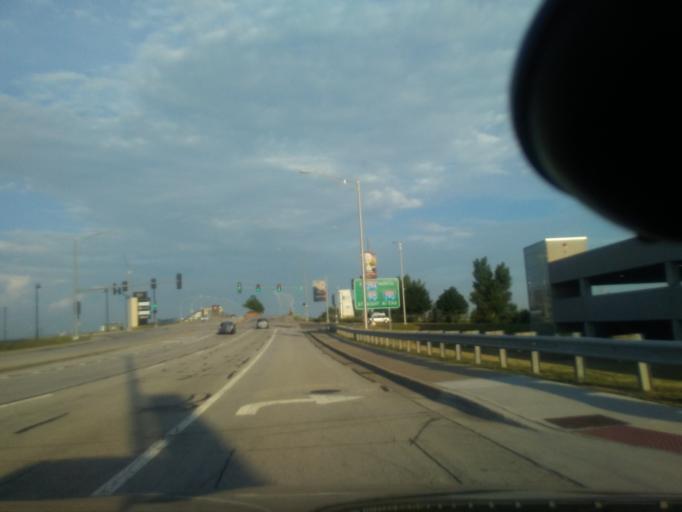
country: US
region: Illinois
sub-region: Cook County
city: Schiller Park
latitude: 41.9766
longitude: -87.8711
